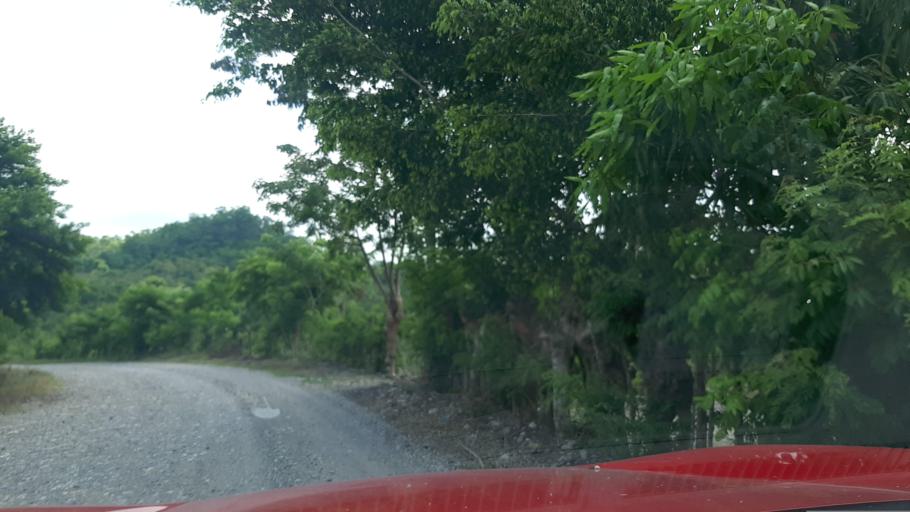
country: MX
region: Veracruz
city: Agua Dulce
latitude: 20.4122
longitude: -97.2817
